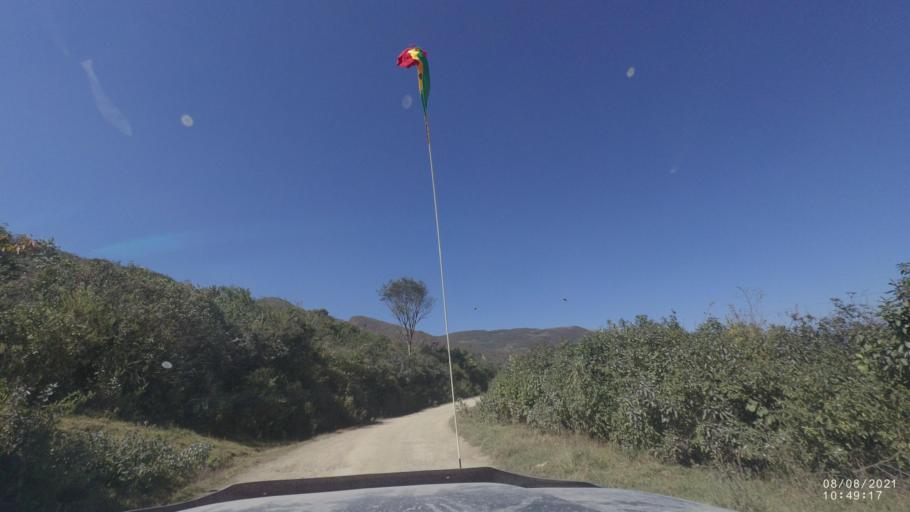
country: BO
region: La Paz
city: Quime
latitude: -16.7192
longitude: -66.7063
